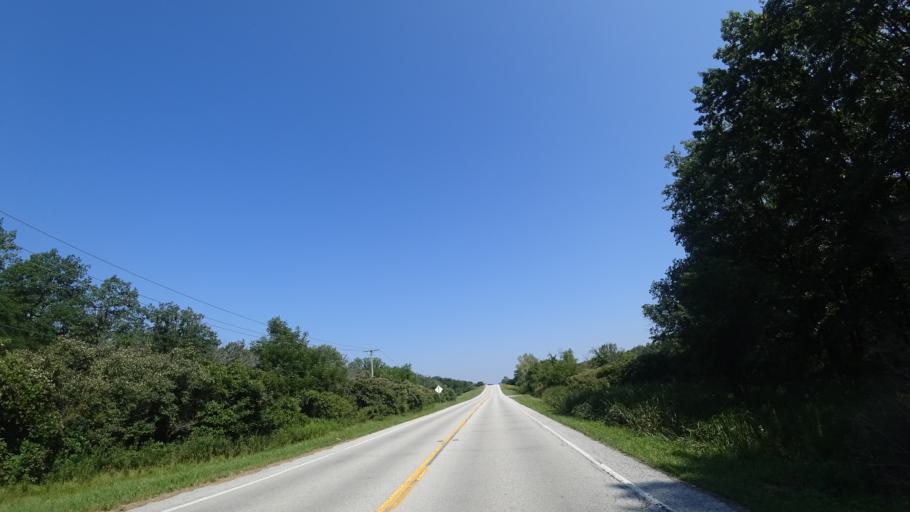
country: US
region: Illinois
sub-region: Cook County
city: Country Club Hills
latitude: 41.5583
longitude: -87.7524
